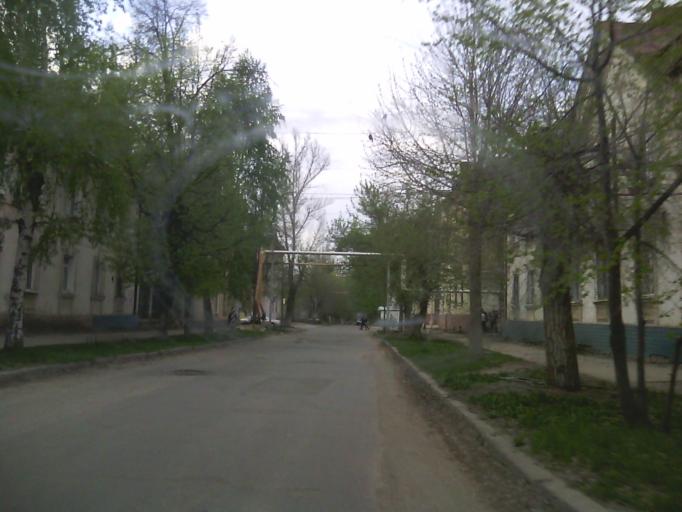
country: RU
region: Saratov
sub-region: Saratovskiy Rayon
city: Saratov
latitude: 51.5875
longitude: 45.9390
